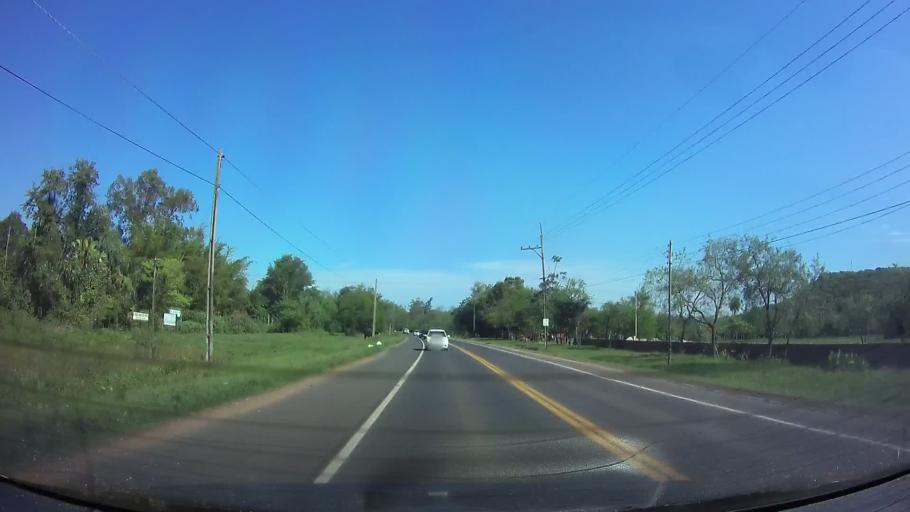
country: PY
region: Central
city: Ypacarai
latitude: -25.3795
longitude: -57.3017
